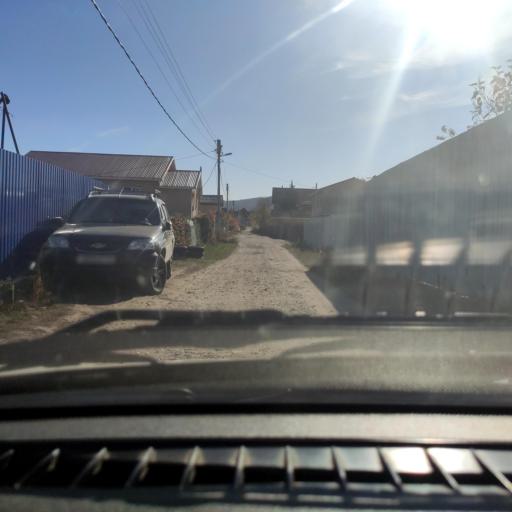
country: RU
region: Samara
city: Zhigulevsk
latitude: 53.4664
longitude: 49.5872
